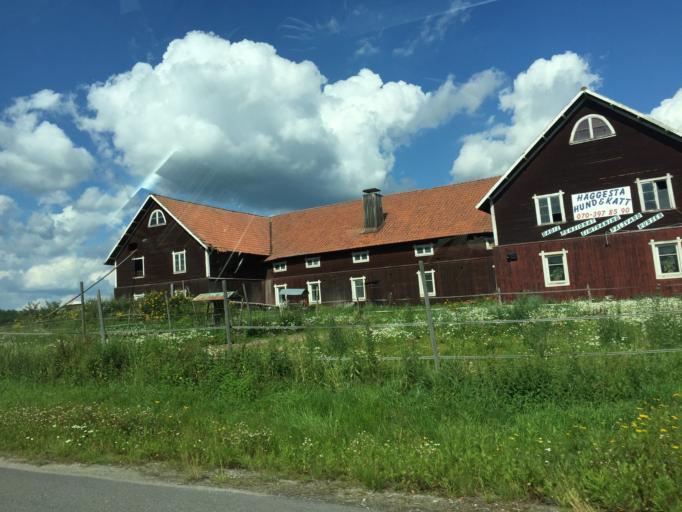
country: SE
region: Gaevleborg
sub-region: Bollnas Kommun
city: Bollnas
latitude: 61.3356
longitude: 16.4009
